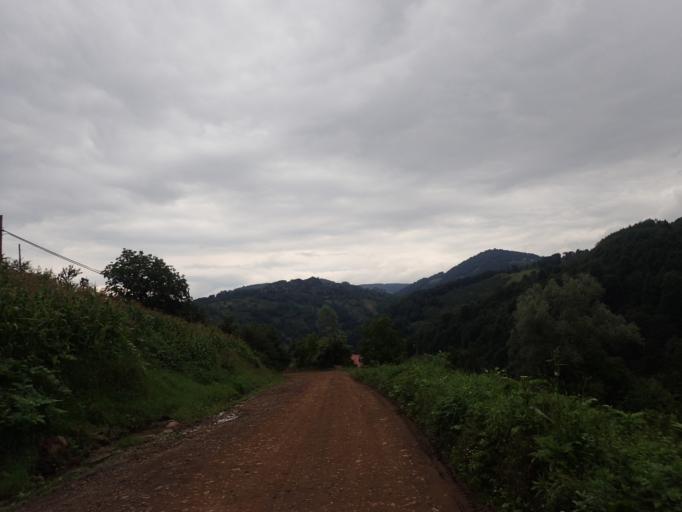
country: TR
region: Ordu
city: Akkus
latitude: 40.8167
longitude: 37.1029
